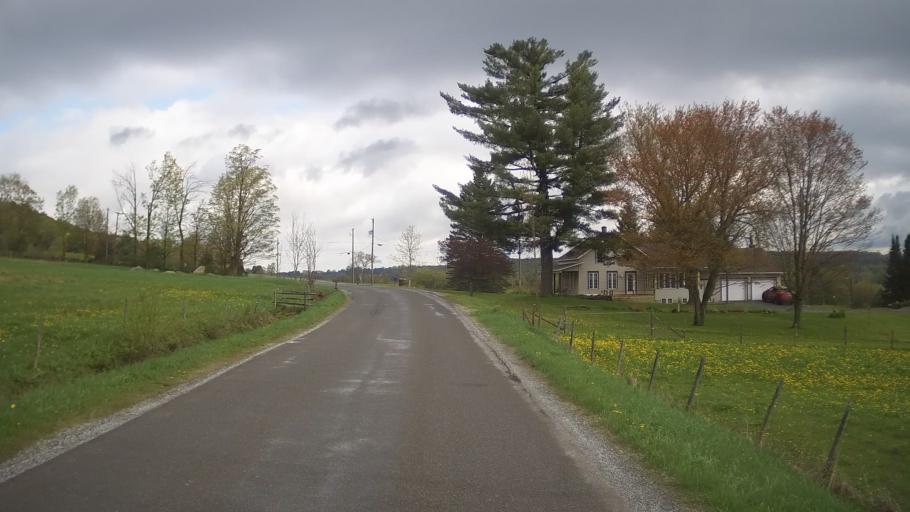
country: CA
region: Quebec
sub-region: Monteregie
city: Cowansville
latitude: 45.1886
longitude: -72.6984
